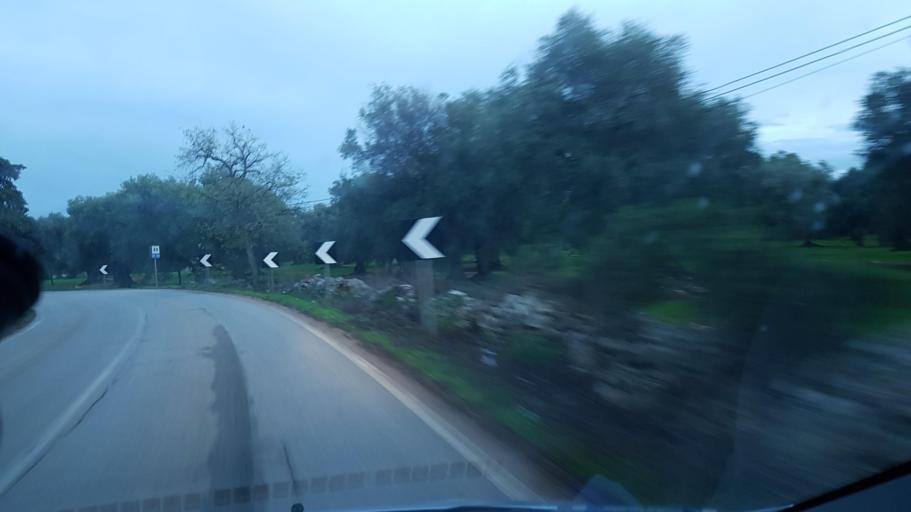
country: IT
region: Apulia
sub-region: Provincia di Brindisi
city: Ceglie Messapica
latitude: 40.6438
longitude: 17.5558
